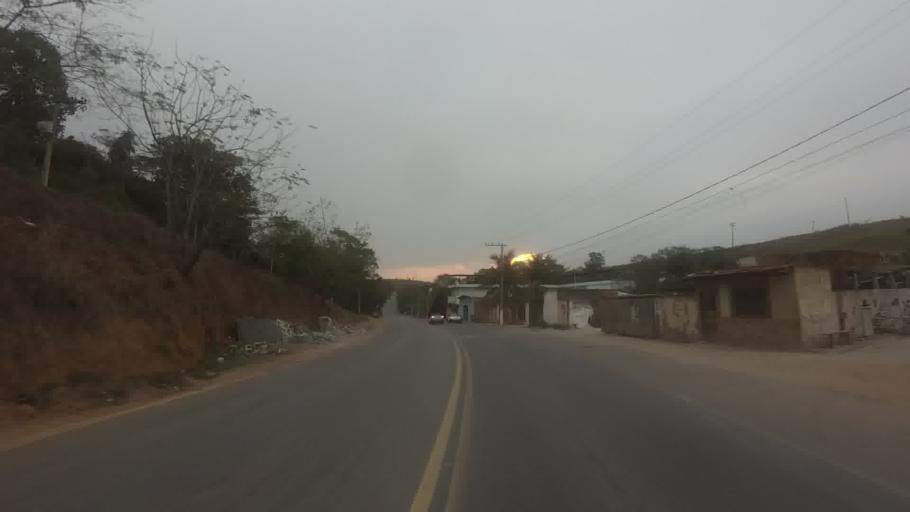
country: BR
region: Minas Gerais
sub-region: Recreio
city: Recreio
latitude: -21.6547
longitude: -42.3568
